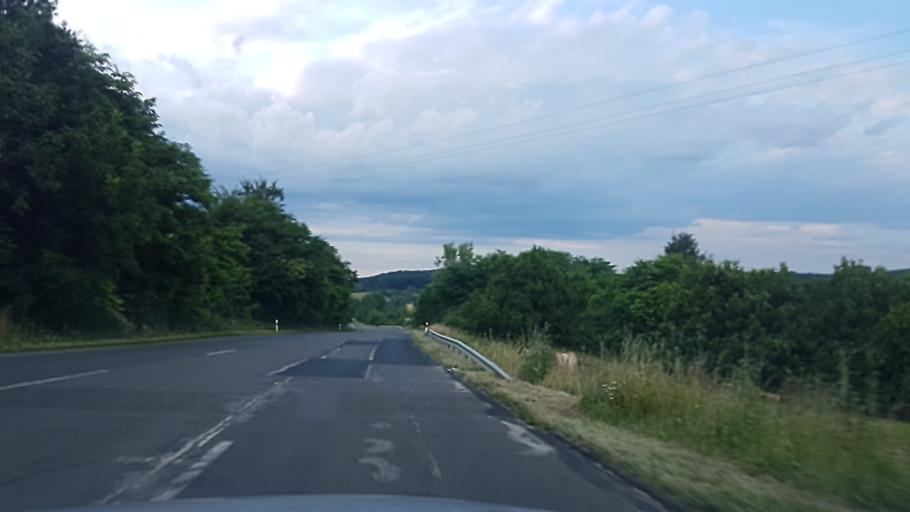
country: HU
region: Somogy
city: Kaposvar
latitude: 46.2765
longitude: 17.8215
